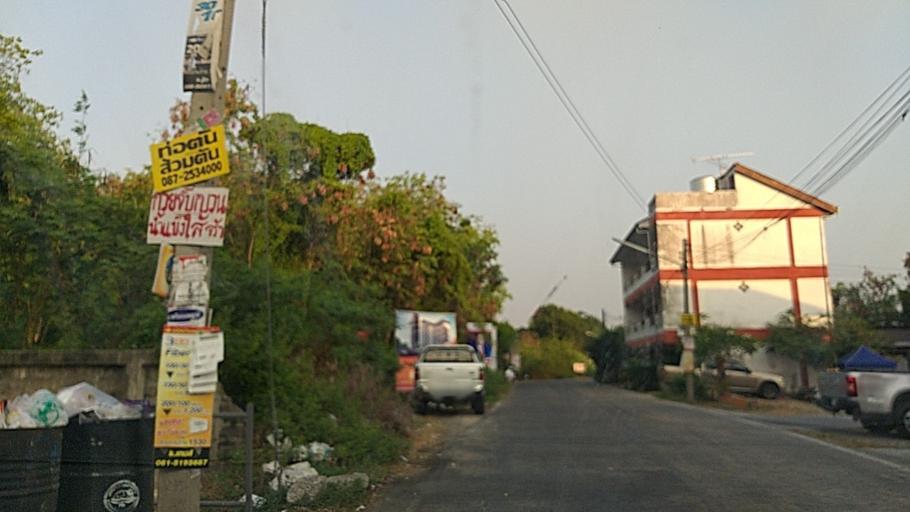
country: TH
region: Phra Nakhon Si Ayutthaya
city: Ban Bang Kadi Pathum Thani
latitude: 13.9958
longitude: 100.5552
